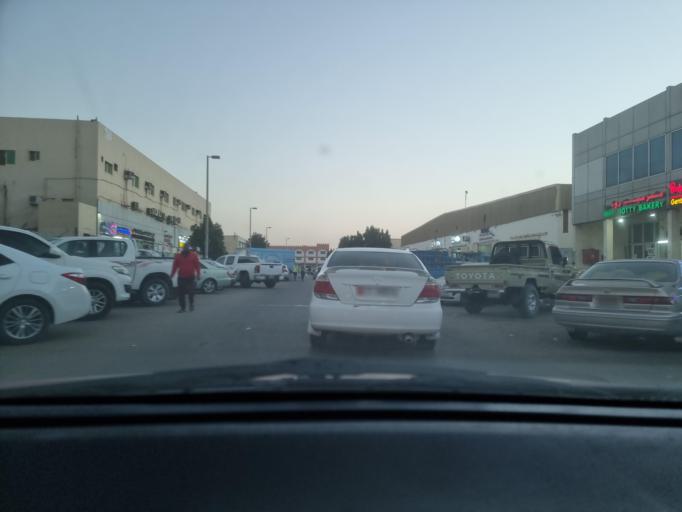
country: AE
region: Abu Dhabi
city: Abu Dhabi
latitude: 24.3505
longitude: 54.5204
